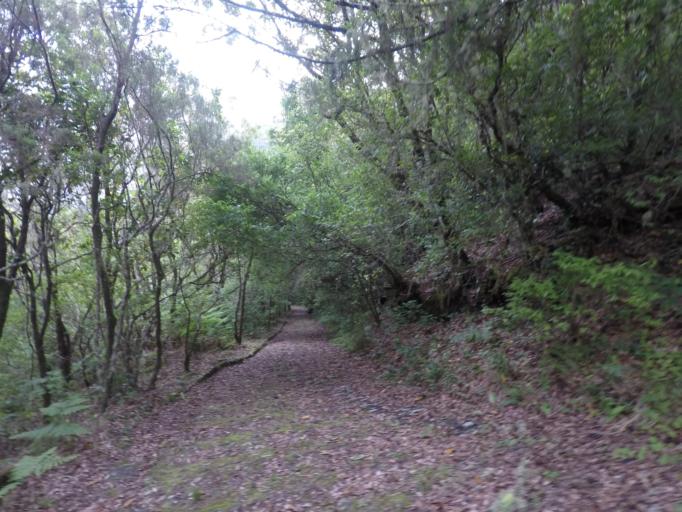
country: PT
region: Madeira
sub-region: Funchal
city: Nossa Senhora do Monte
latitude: 32.7323
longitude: -16.8880
